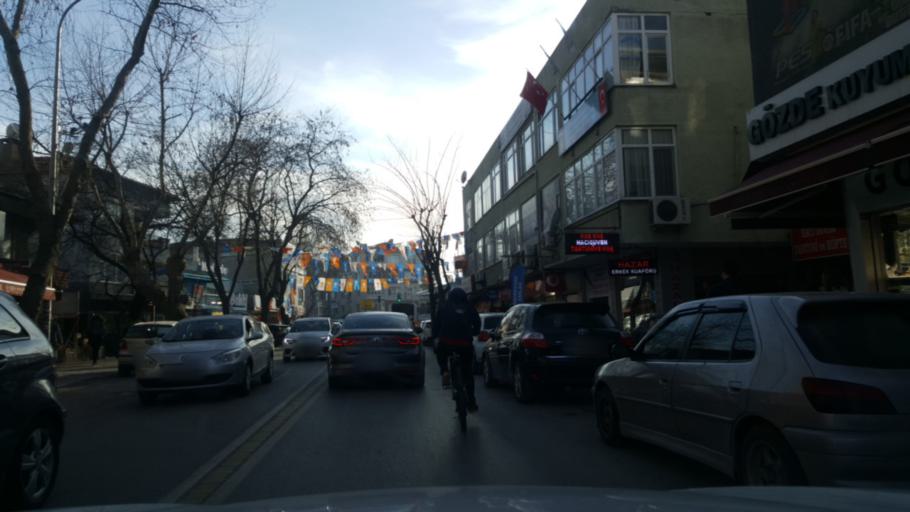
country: TR
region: Istanbul
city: Icmeler
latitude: 40.8183
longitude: 29.3052
